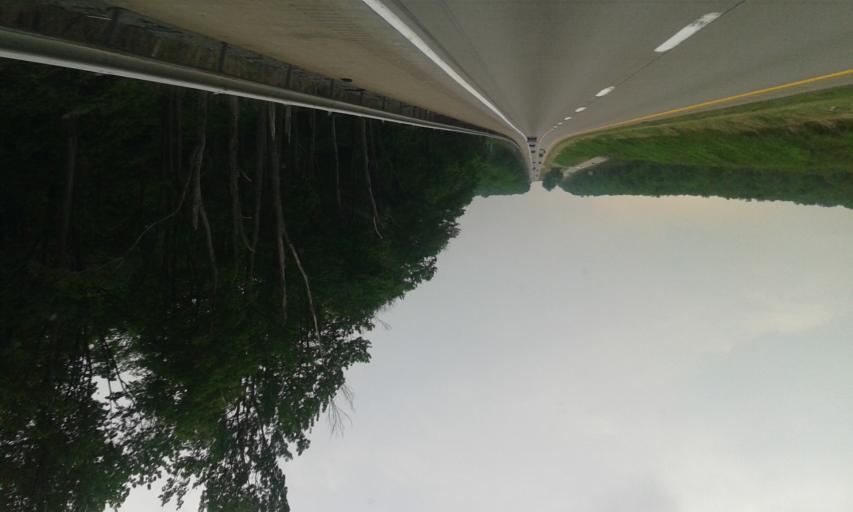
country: US
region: Pennsylvania
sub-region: Monroe County
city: Pocono Pines
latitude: 41.2007
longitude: -75.4557
